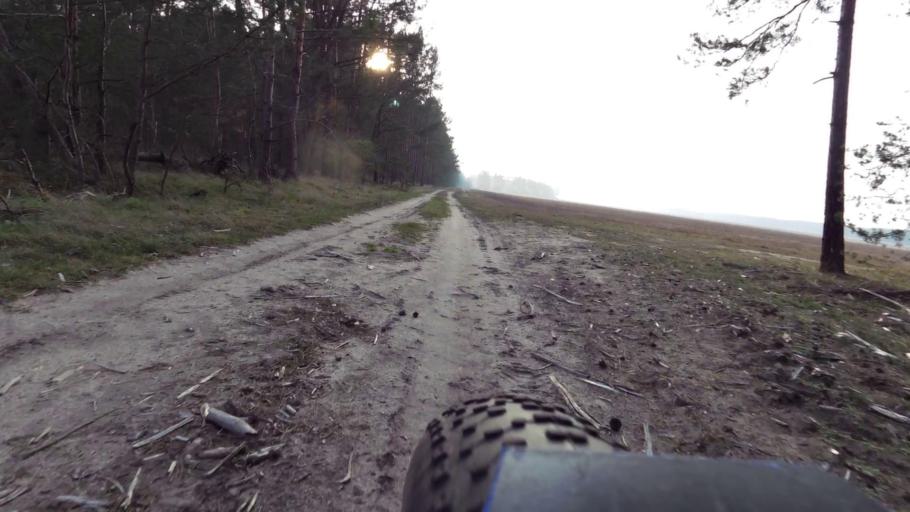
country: DE
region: Brandenburg
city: Vogelsang
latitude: 52.2684
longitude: 14.6893
